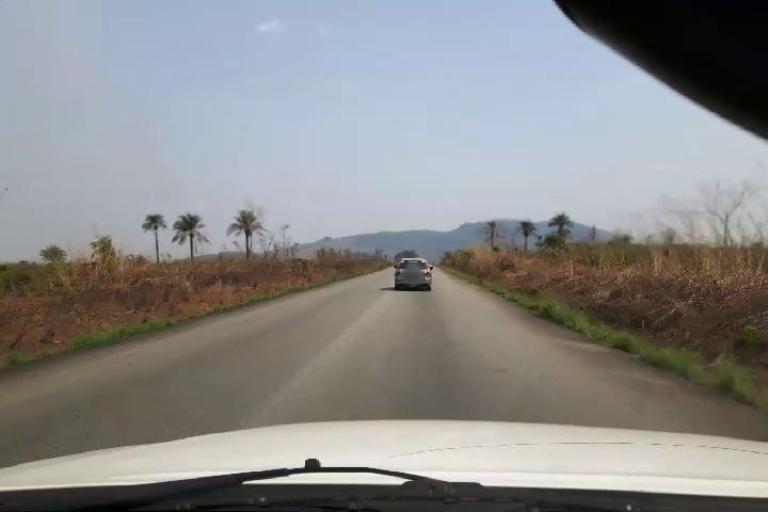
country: SL
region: Northern Province
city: Yonibana
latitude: 8.3916
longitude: -12.1921
